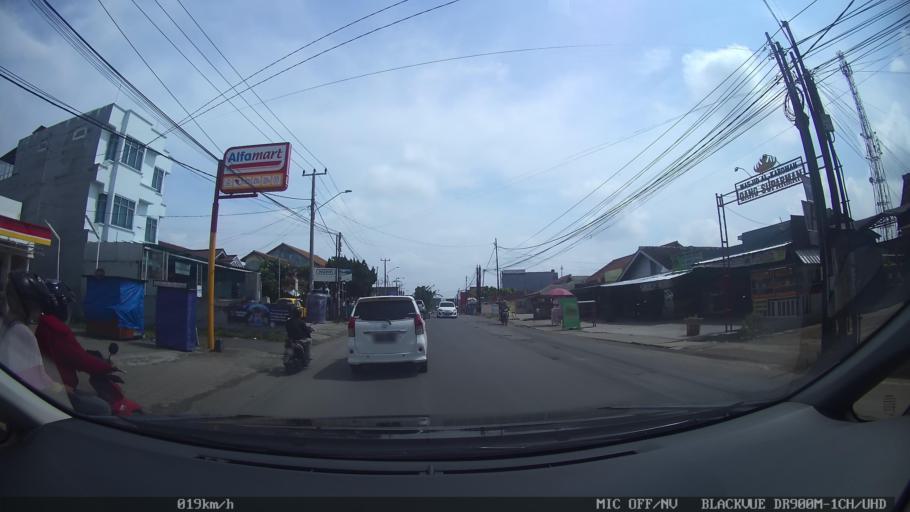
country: ID
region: Lampung
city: Kedaton
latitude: -5.3682
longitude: 105.2749
